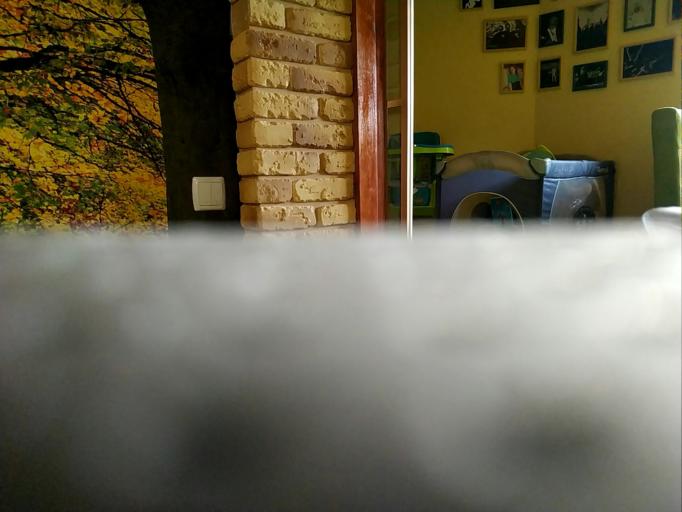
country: RU
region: Kaluga
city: Seredeyskiy
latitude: 53.9609
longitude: 35.3323
